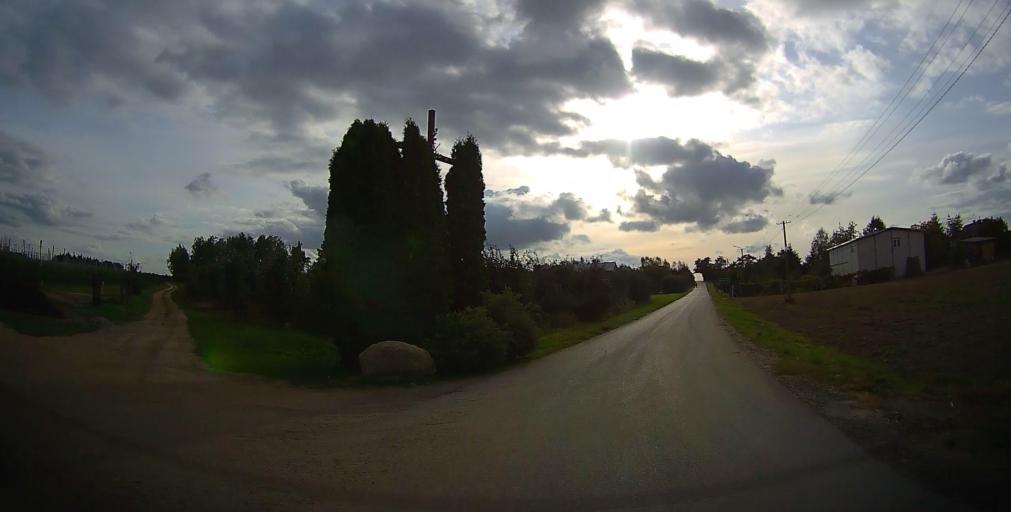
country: PL
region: Masovian Voivodeship
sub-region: Powiat grojecki
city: Jasieniec
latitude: 51.7715
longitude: 20.9210
